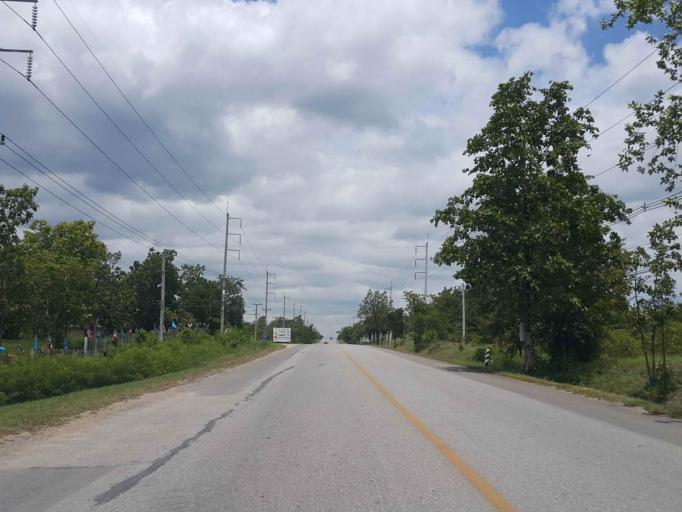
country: TH
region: Lamphun
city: Ban Hong
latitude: 18.3655
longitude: 98.8122
